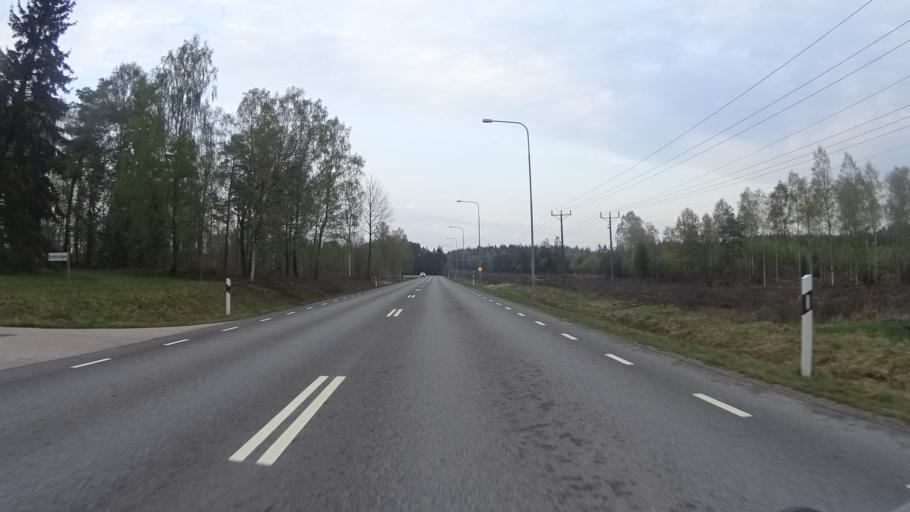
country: SE
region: Kronoberg
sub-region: Ljungby Kommun
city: Ljungby
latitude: 56.8291
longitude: 13.9715
